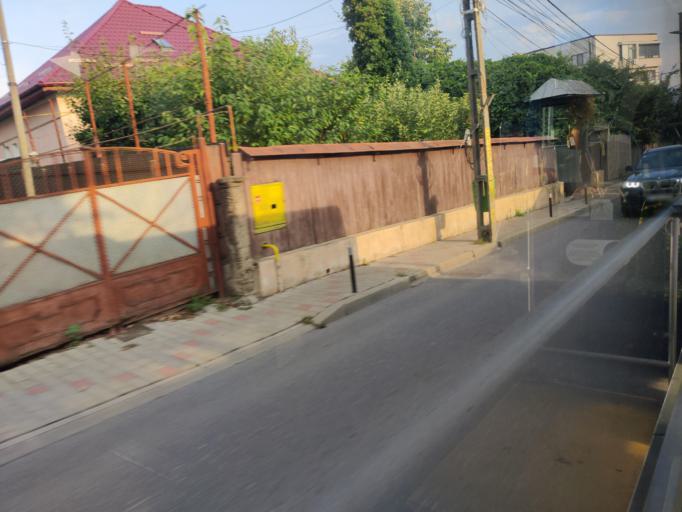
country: RO
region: Iasi
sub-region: Municipiul Iasi
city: Iasi
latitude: 47.1694
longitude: 27.5999
